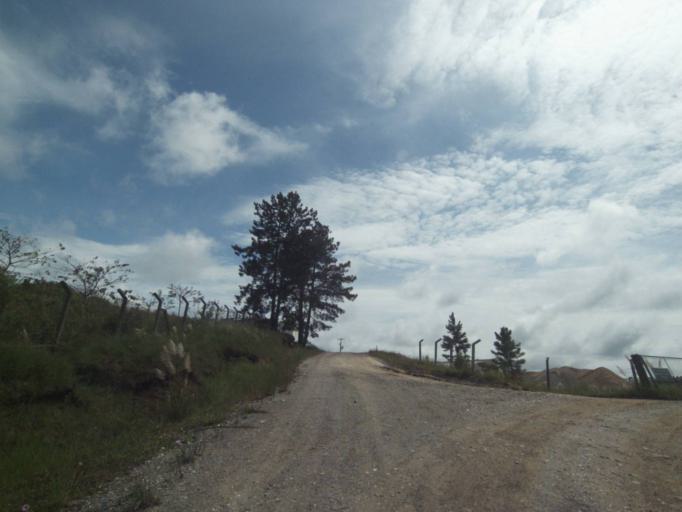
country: BR
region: Parana
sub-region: Campina Grande Do Sul
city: Campina Grande do Sul
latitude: -25.3088
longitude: -49.0585
